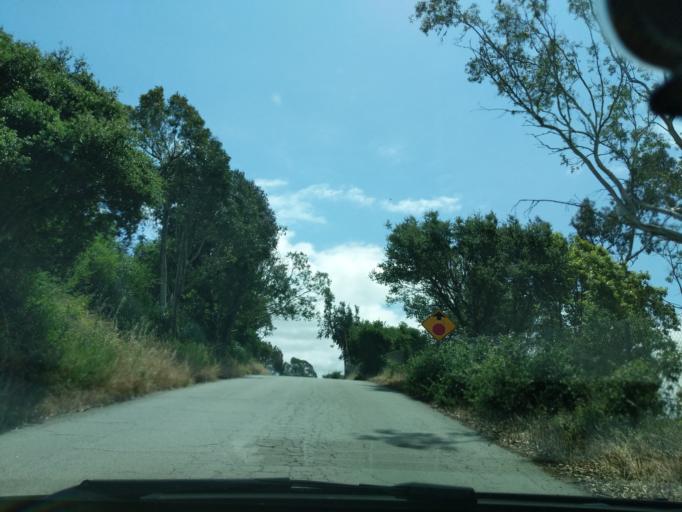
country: US
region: California
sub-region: Santa Cruz County
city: Freedom
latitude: 36.9262
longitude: -121.7990
